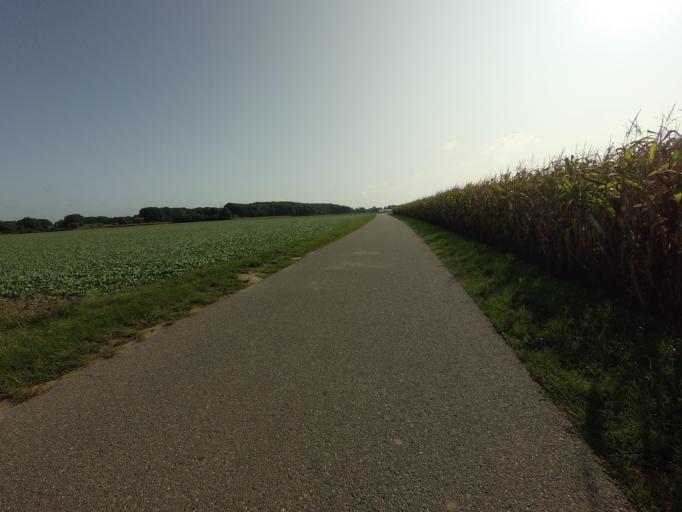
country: NL
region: Limburg
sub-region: Gemeente Roerdalen
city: Melick
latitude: 51.1521
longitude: 6.0289
